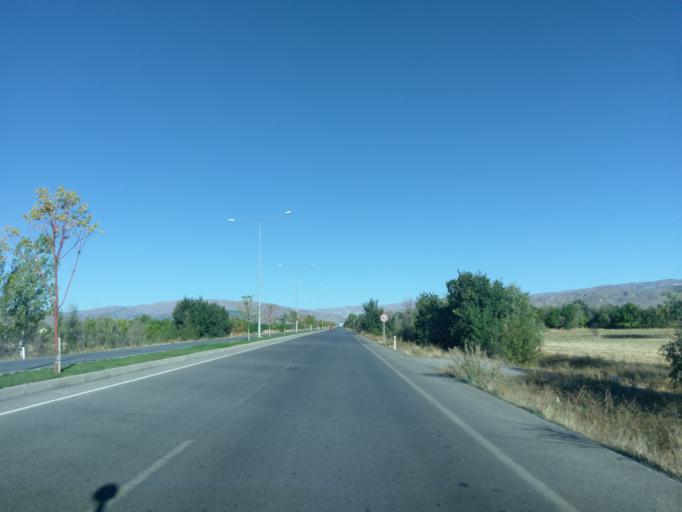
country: TR
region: Erzincan
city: Erzincan
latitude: 39.7772
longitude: 39.4151
